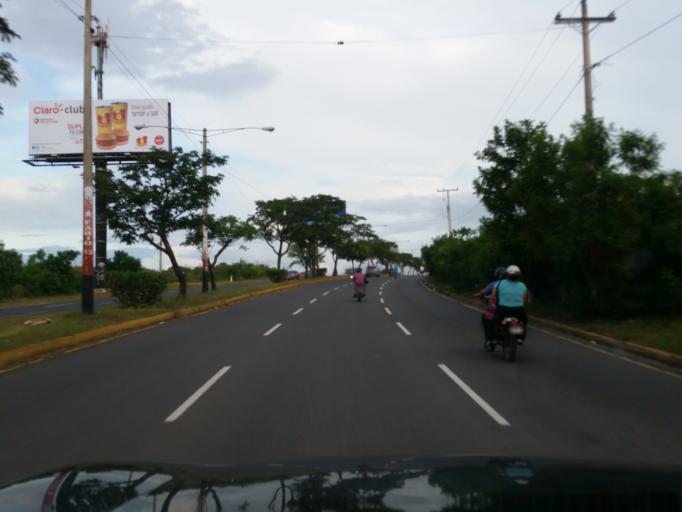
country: NI
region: Managua
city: Managua
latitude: 12.1113
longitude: -86.3046
